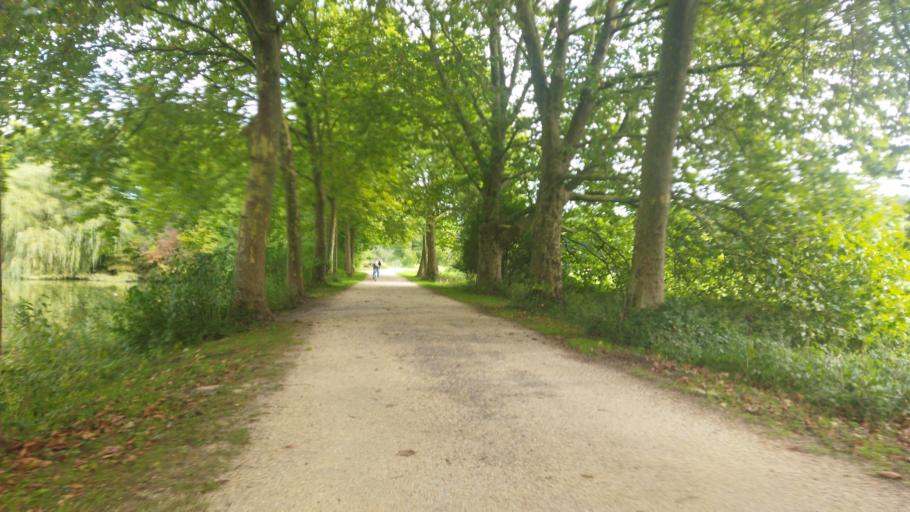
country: DE
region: North Rhine-Westphalia
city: Herten
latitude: 51.5897
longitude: 7.1287
